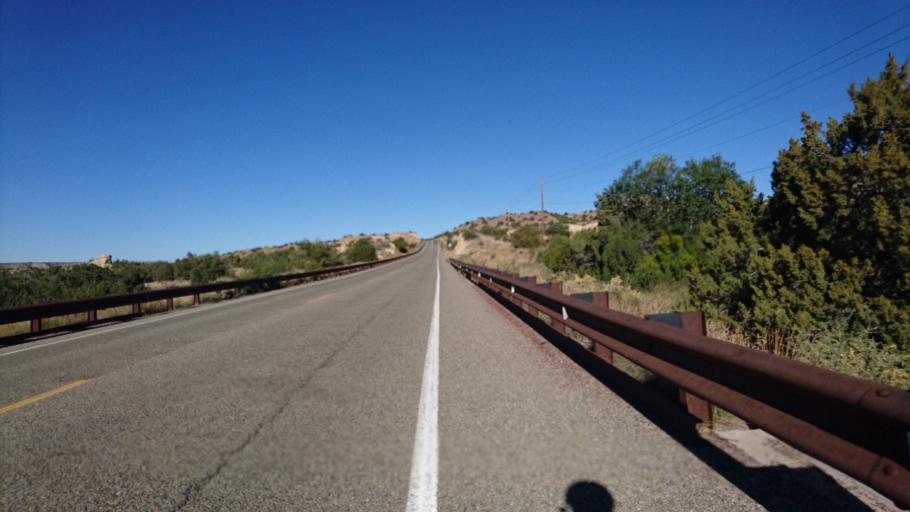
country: US
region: New Mexico
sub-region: Santa Fe County
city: La Cienega
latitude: 35.4325
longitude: -106.1013
